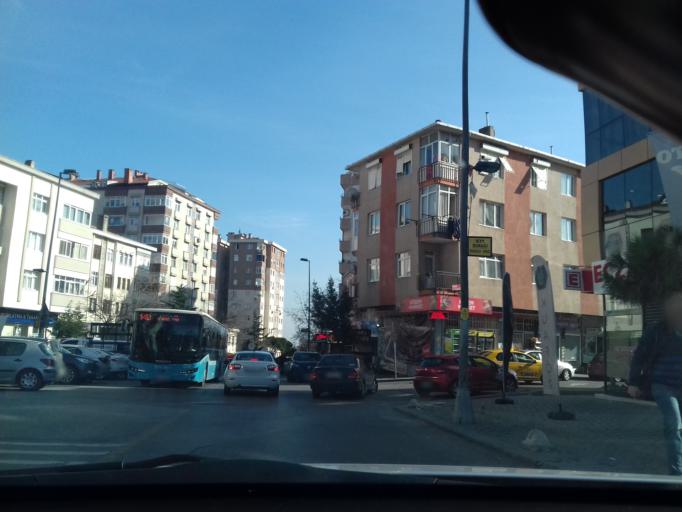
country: TR
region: Istanbul
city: Umraniye
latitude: 41.0228
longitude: 29.0806
